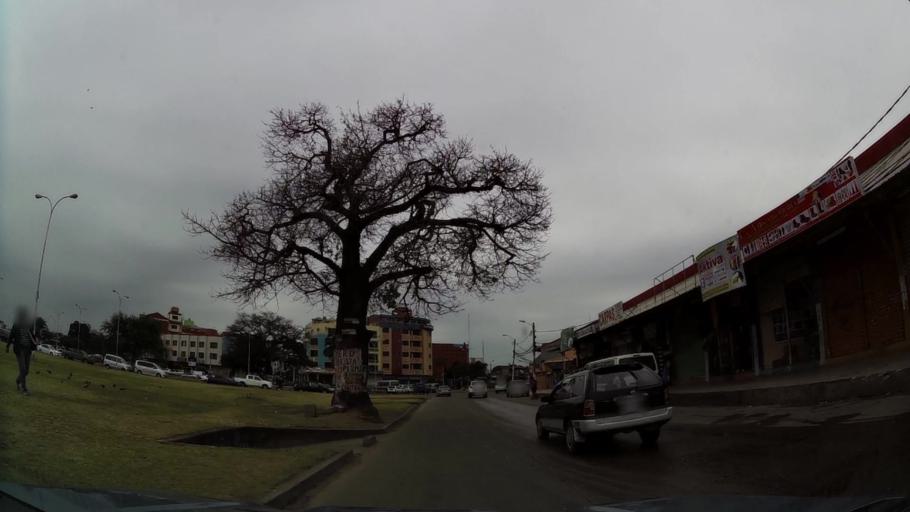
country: BO
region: Santa Cruz
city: Santa Cruz de la Sierra
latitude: -17.7872
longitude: -63.1620
